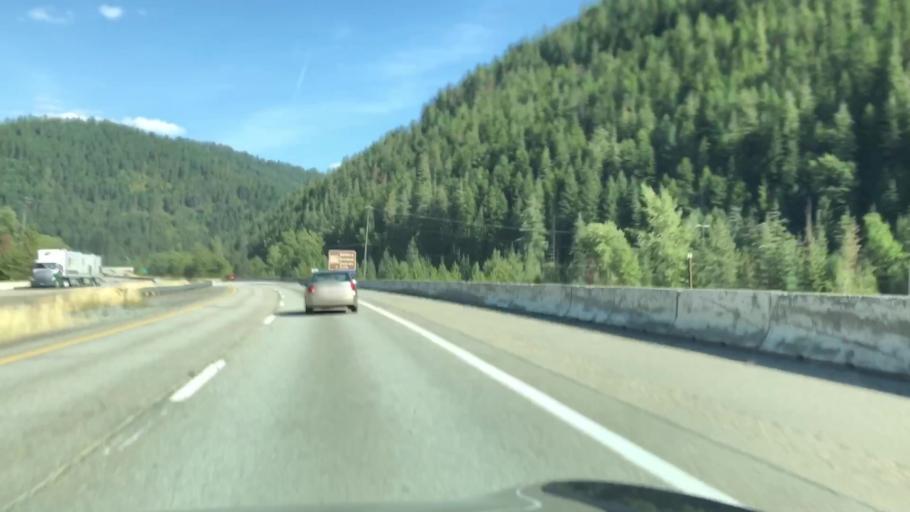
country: US
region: Idaho
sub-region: Shoshone County
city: Osburn
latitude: 47.4911
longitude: -115.9688
